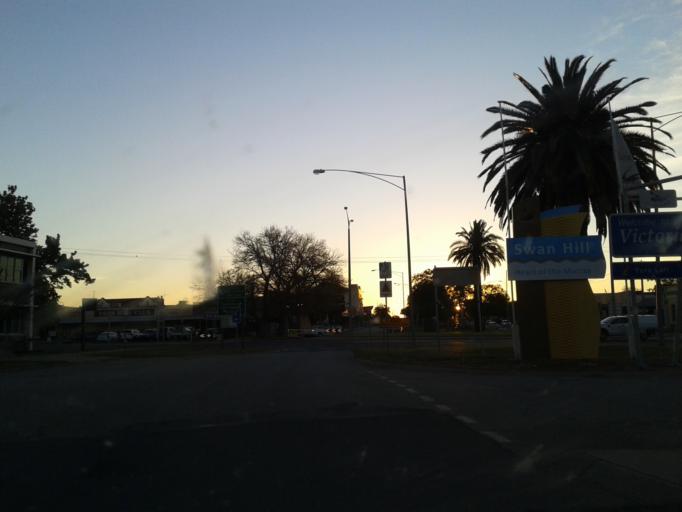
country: AU
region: Victoria
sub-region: Swan Hill
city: Swan Hill
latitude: -35.3383
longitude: 143.5616
